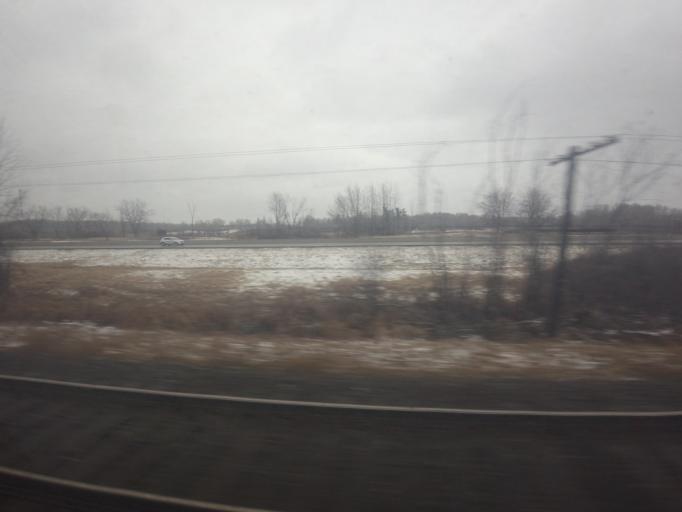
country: CA
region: Ontario
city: Kingston
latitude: 44.3183
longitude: -76.3708
